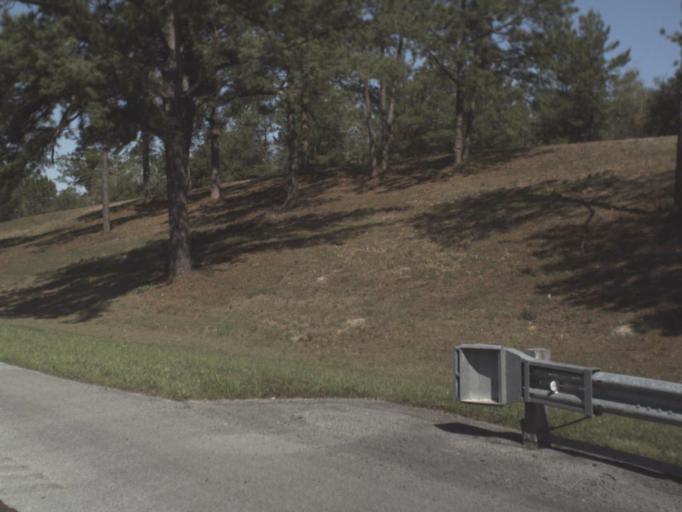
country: US
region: Florida
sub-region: Walton County
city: DeFuniak Springs
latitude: 30.7249
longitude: -86.2016
